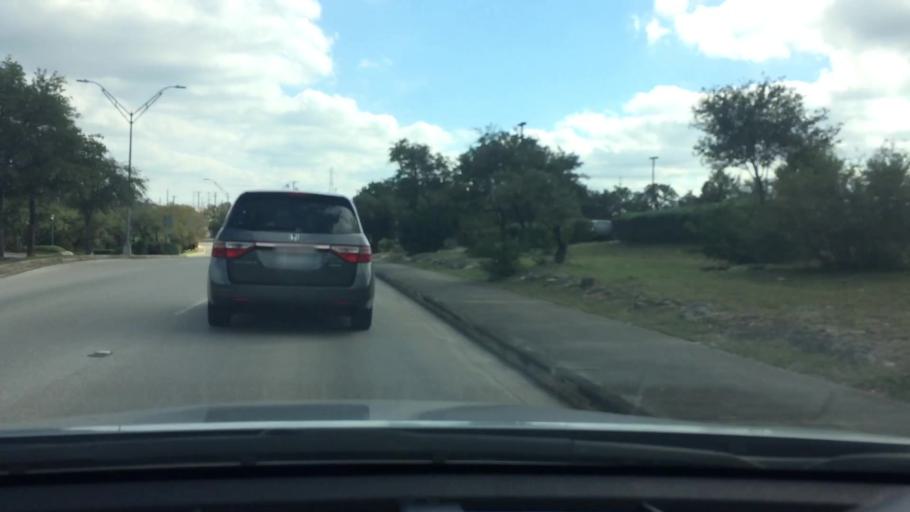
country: US
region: Texas
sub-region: Bexar County
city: Shavano Park
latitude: 29.5796
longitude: -98.5660
